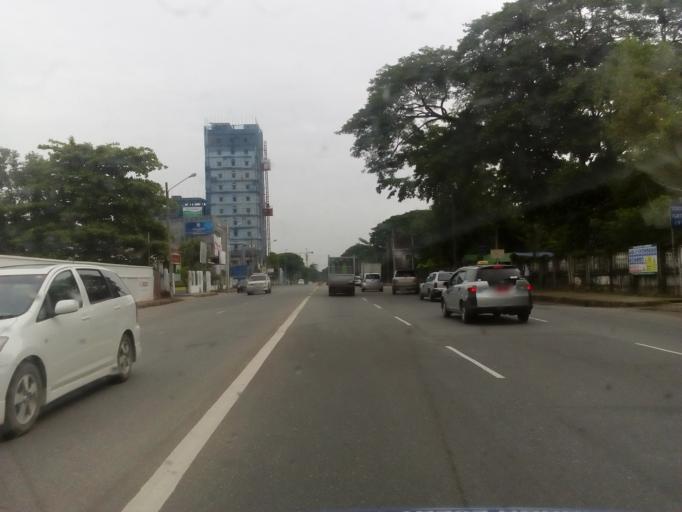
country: MM
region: Yangon
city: Yangon
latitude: 16.8449
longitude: 96.1568
